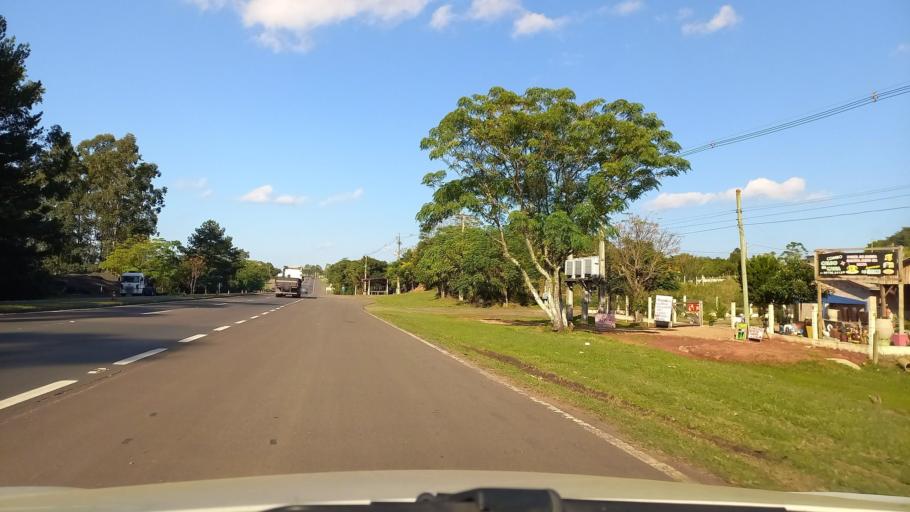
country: BR
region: Rio Grande do Sul
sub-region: Taquari
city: Taquari
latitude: -29.6929
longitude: -51.7010
